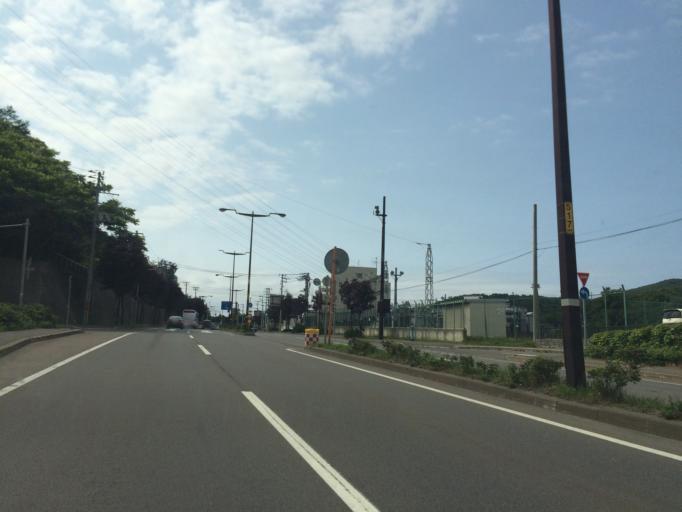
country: JP
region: Hokkaido
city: Otaru
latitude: 43.2060
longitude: 140.9814
